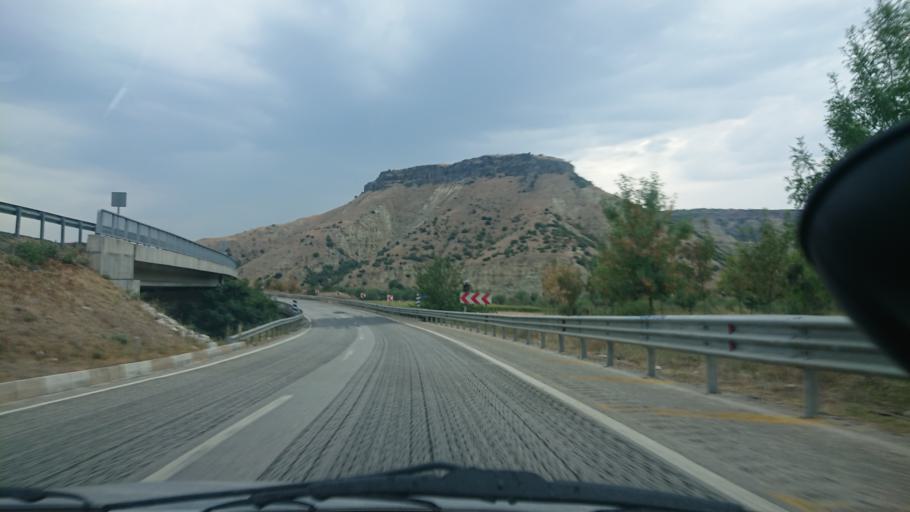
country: TR
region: Manisa
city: Selendi
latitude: 38.6019
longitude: 28.8163
